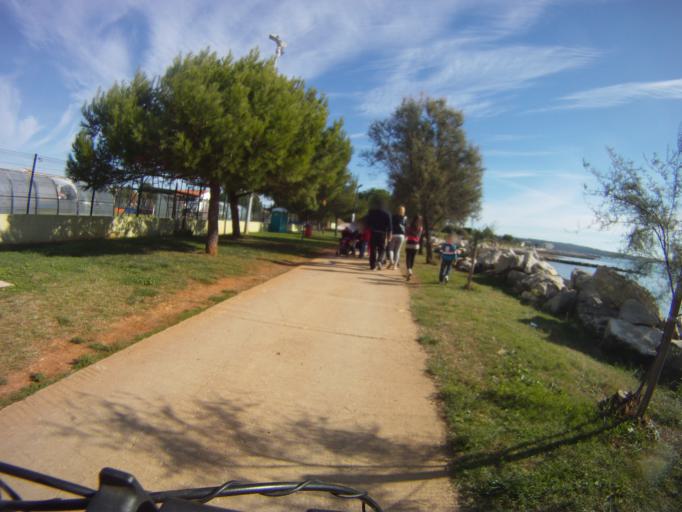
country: HR
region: Istarska
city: Novigrad
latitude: 45.3163
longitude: 13.5679
